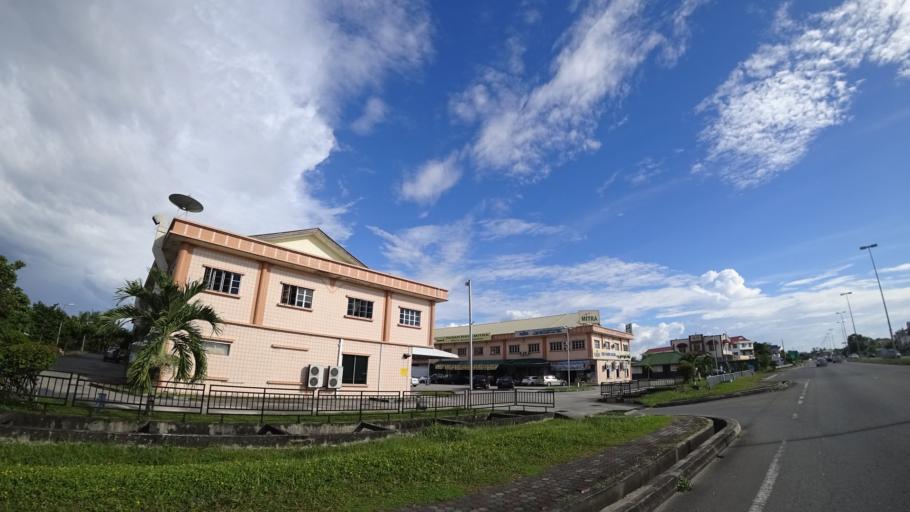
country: BN
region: Brunei and Muara
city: Bandar Seri Begawan
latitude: 4.8928
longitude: 114.8473
